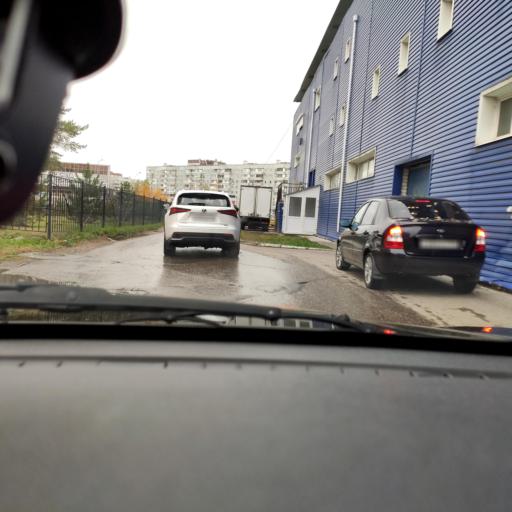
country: RU
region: Samara
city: Tol'yatti
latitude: 53.5385
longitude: 49.3608
